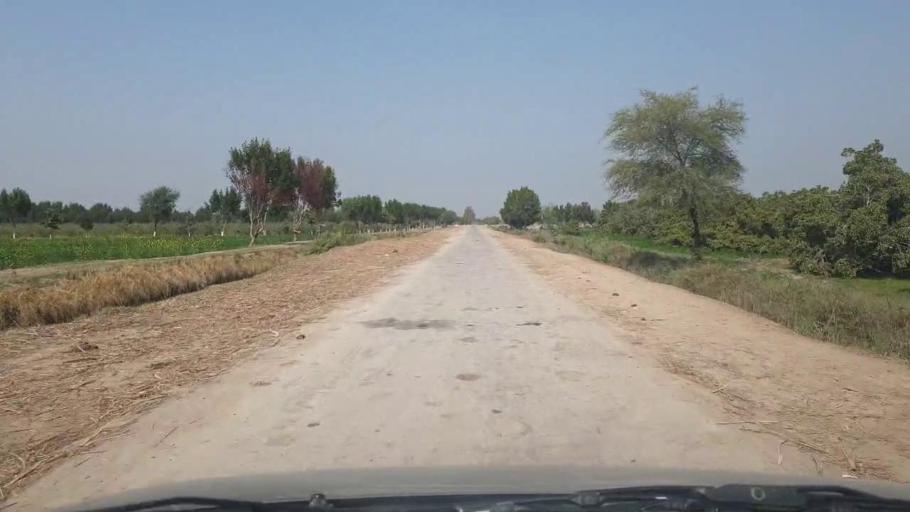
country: PK
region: Sindh
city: Mirwah Gorchani
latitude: 25.3618
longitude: 69.1442
